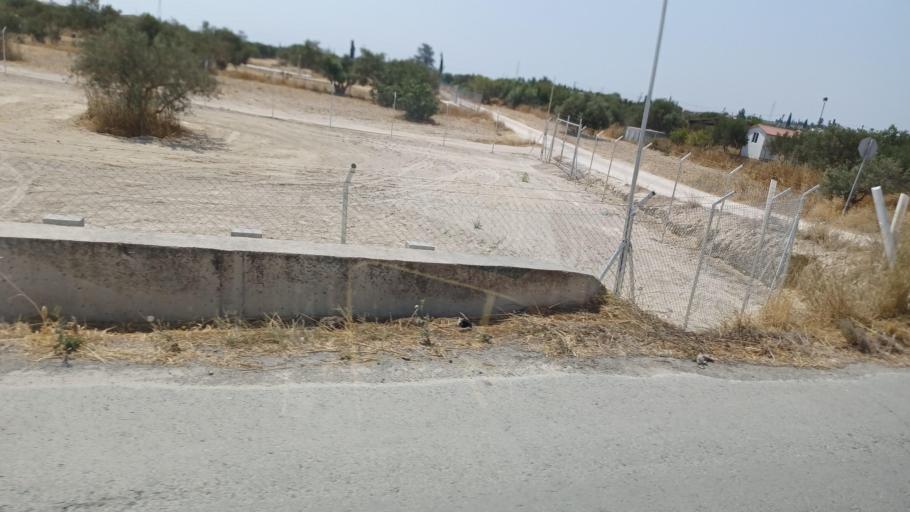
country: CY
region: Larnaka
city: Aradippou
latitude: 34.9610
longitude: 33.6059
